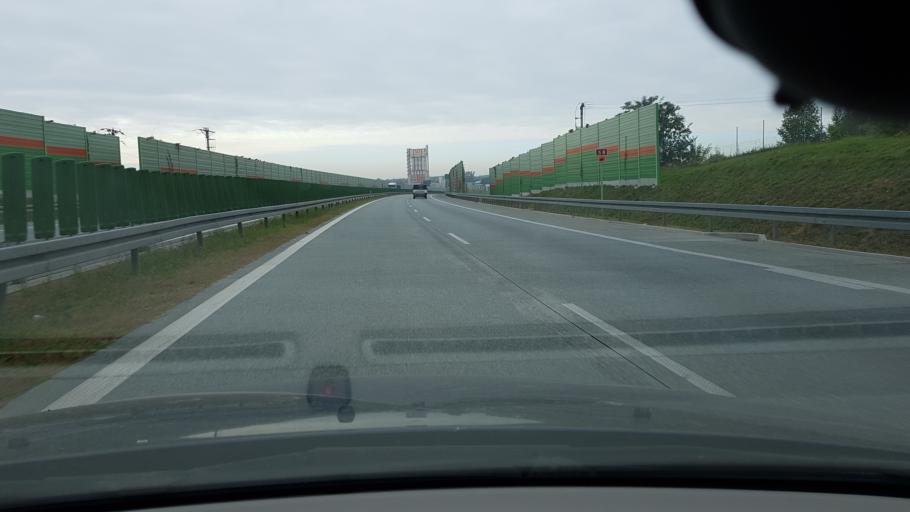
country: PL
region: Lodz Voivodeship
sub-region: Powiat rawski
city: Rawa Mazowiecka
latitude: 51.7689
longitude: 20.2724
